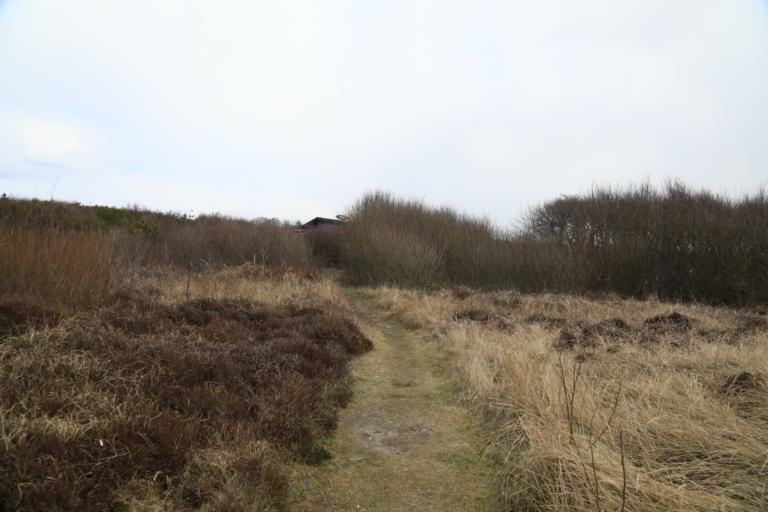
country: SE
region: Halland
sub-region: Varbergs Kommun
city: Traslovslage
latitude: 57.0775
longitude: 12.2623
